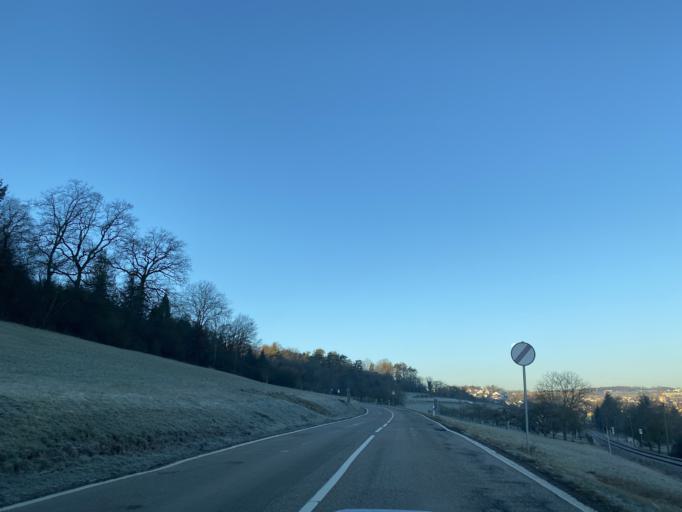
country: DE
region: Baden-Wuerttemberg
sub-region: Regierungsbezirk Stuttgart
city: Weissach
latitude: 48.8466
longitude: 8.9442
